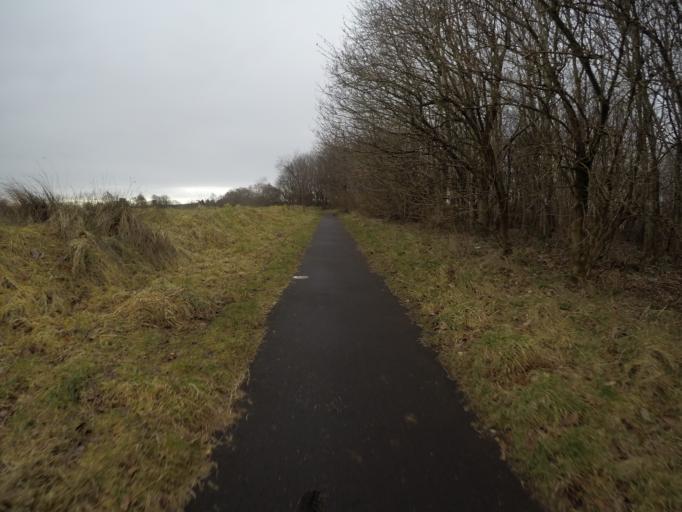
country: GB
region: Scotland
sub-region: North Ayrshire
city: Kilwinning
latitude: 55.6440
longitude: -4.6973
